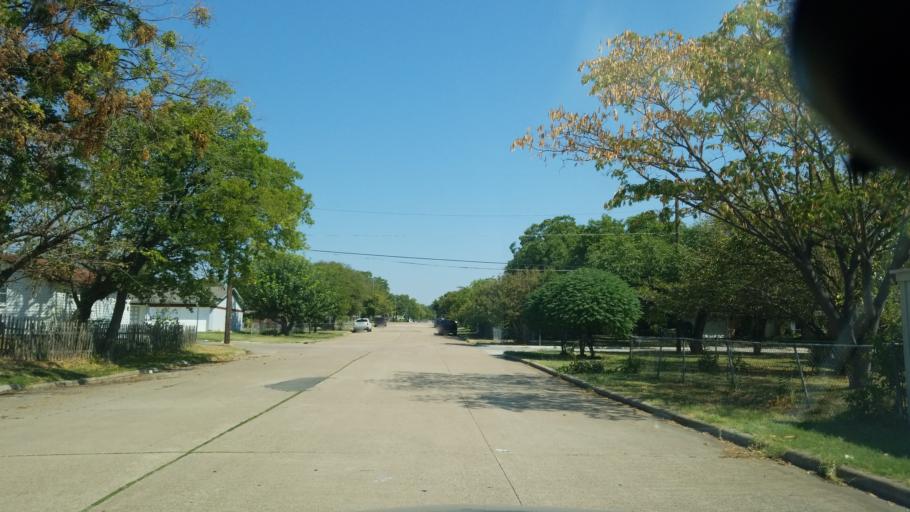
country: US
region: Texas
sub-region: Dallas County
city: Grand Prairie
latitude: 32.7075
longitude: -96.9815
